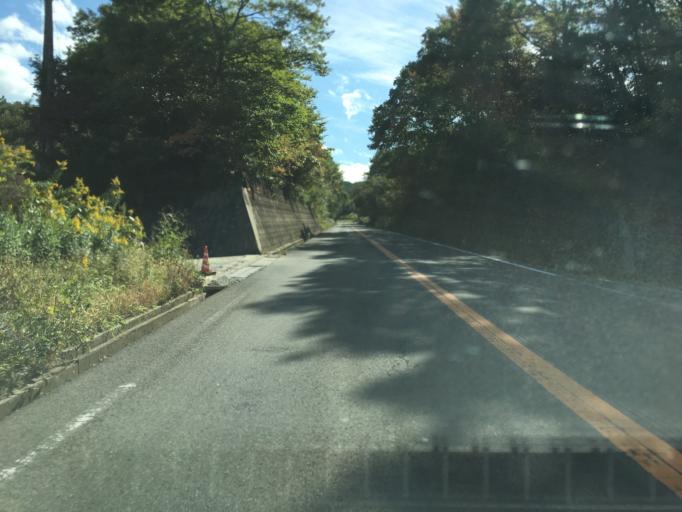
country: JP
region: Fukushima
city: Fukushima-shi
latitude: 37.7550
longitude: 140.5214
